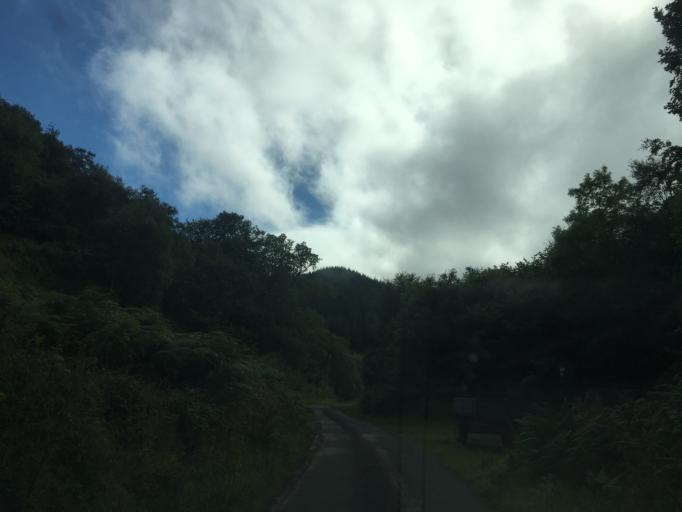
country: GB
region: Scotland
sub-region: Argyll and Bute
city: Ardrishaig
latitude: 56.0879
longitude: -5.5586
